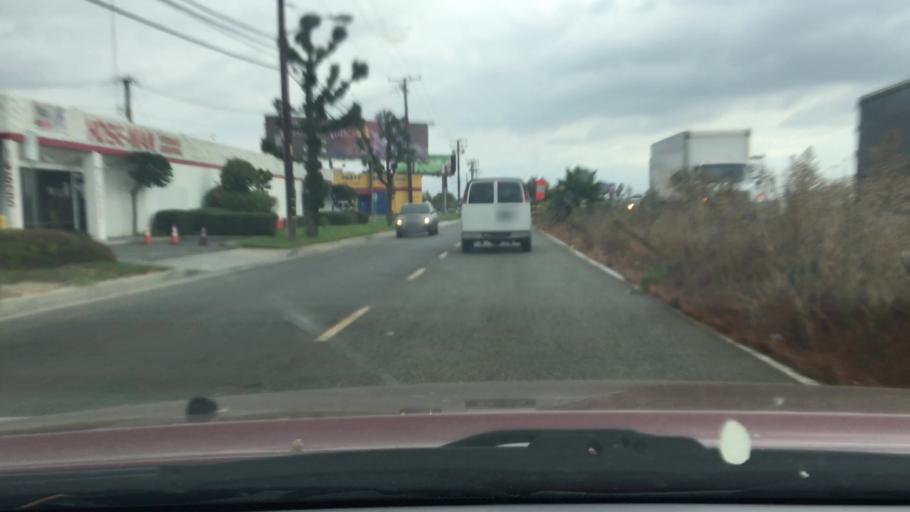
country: US
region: California
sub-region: Orange County
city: Buena Park
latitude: 33.8809
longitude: -118.0225
